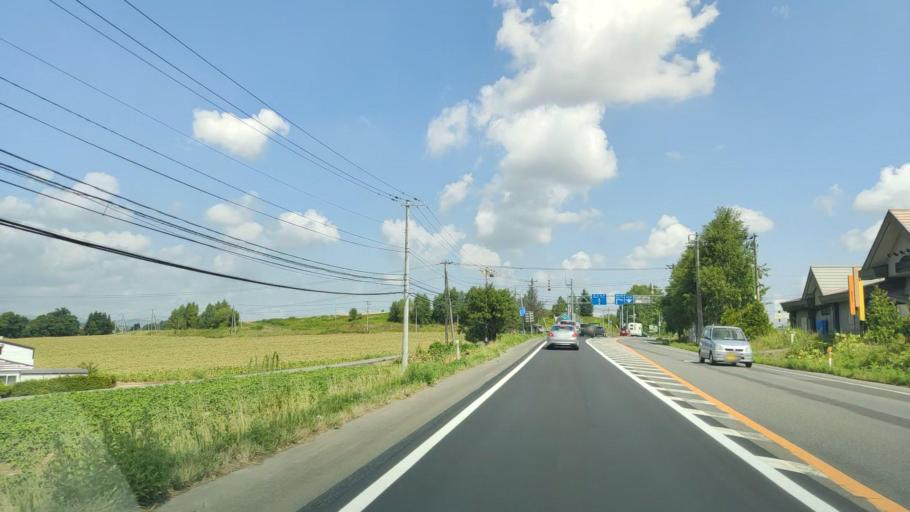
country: JP
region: Hokkaido
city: Shimo-furano
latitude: 43.5440
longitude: 142.4386
